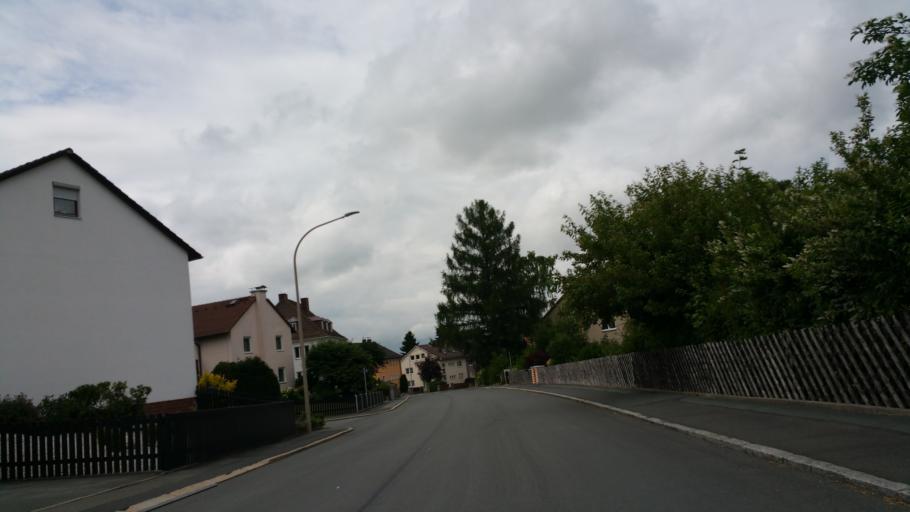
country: DE
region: Bavaria
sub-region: Upper Franconia
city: Rehau
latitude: 50.2400
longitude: 12.0371
